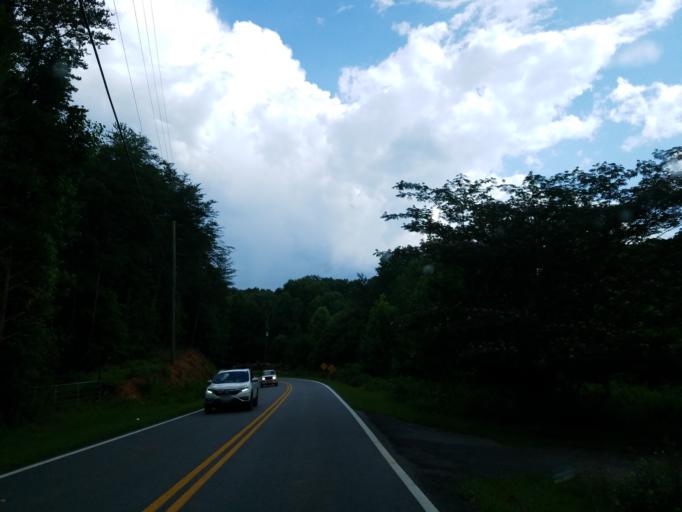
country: US
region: Georgia
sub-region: Gilmer County
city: Ellijay
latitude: 34.6718
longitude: -84.3676
